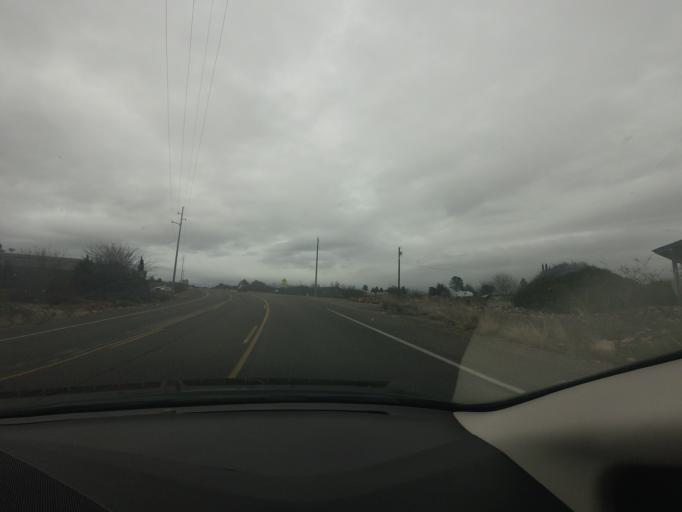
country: US
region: Arizona
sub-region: Yavapai County
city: Lake Montezuma
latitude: 34.6454
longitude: -111.7853
